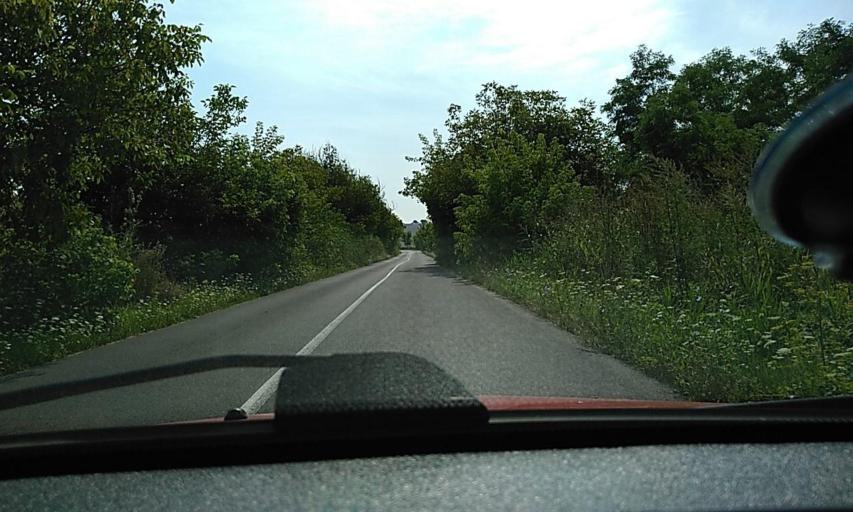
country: RO
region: Brasov
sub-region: Oras Rupea
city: Rupea
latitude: 46.0202
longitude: 25.1883
